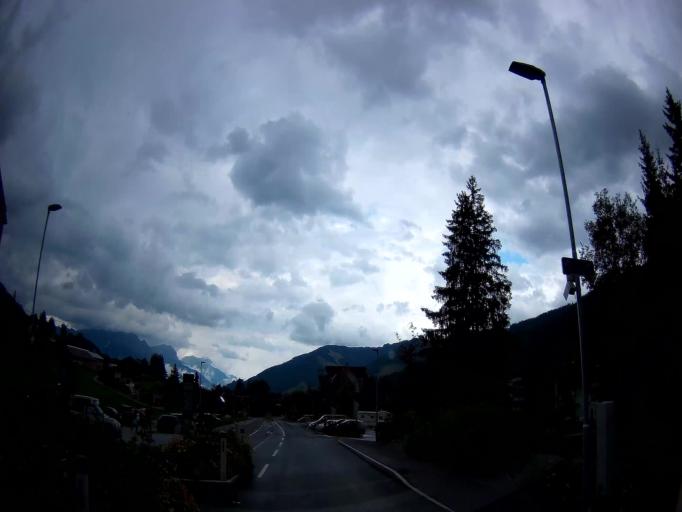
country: AT
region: Salzburg
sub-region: Politischer Bezirk Zell am See
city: Leogang
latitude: 47.4408
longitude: 12.7167
